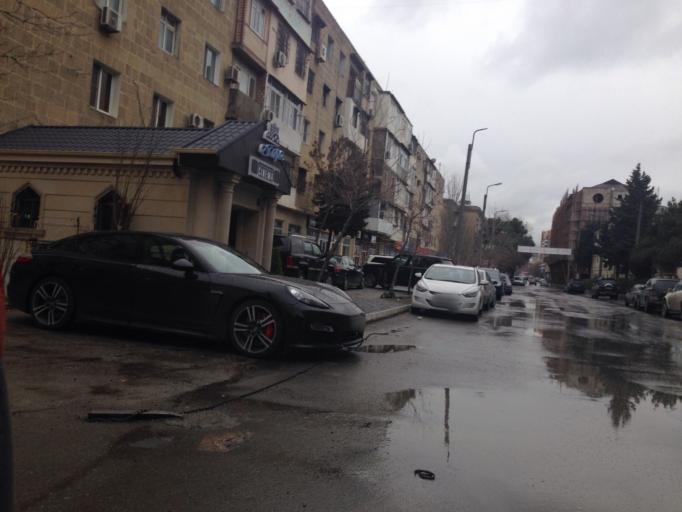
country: AZ
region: Baki
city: Baku
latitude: 40.4079
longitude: 49.8736
